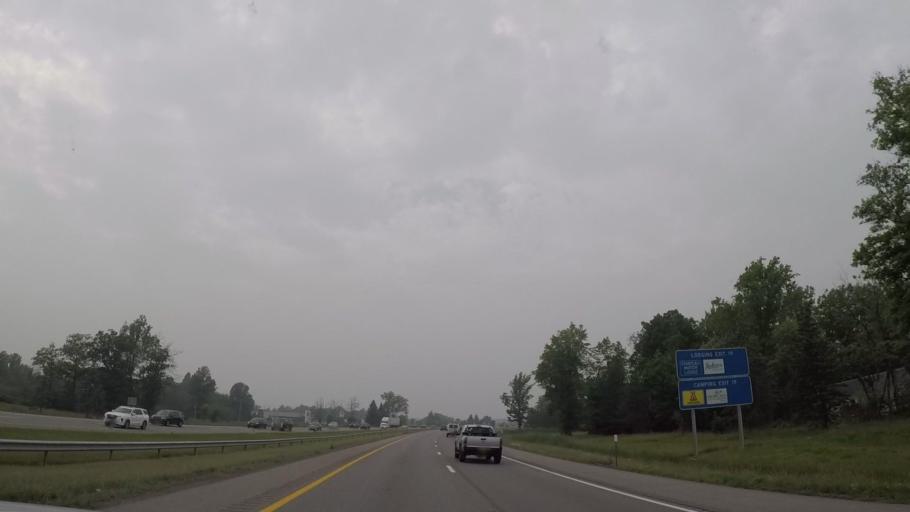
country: US
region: New York
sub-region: Erie County
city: Grandyle Village
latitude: 43.0135
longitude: -78.9677
